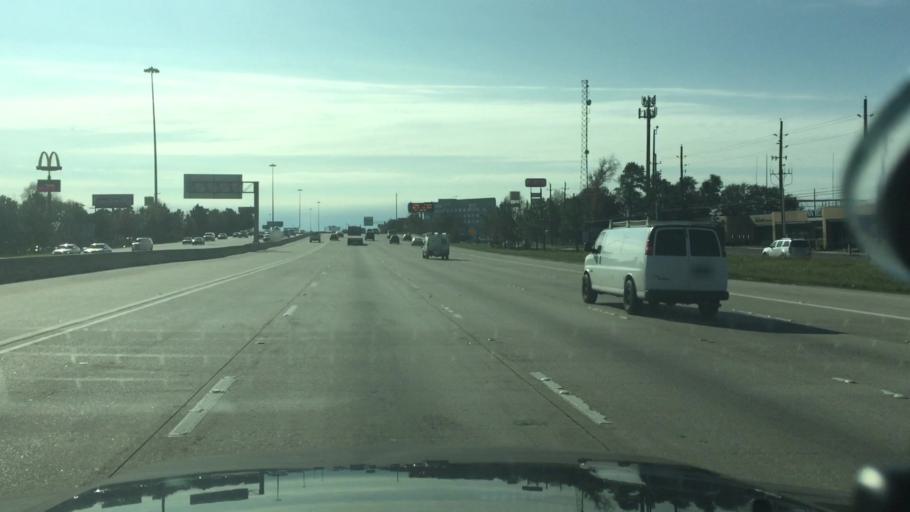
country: US
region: Texas
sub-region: Montgomery County
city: Oak Ridge North
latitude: 30.1302
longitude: -95.4442
